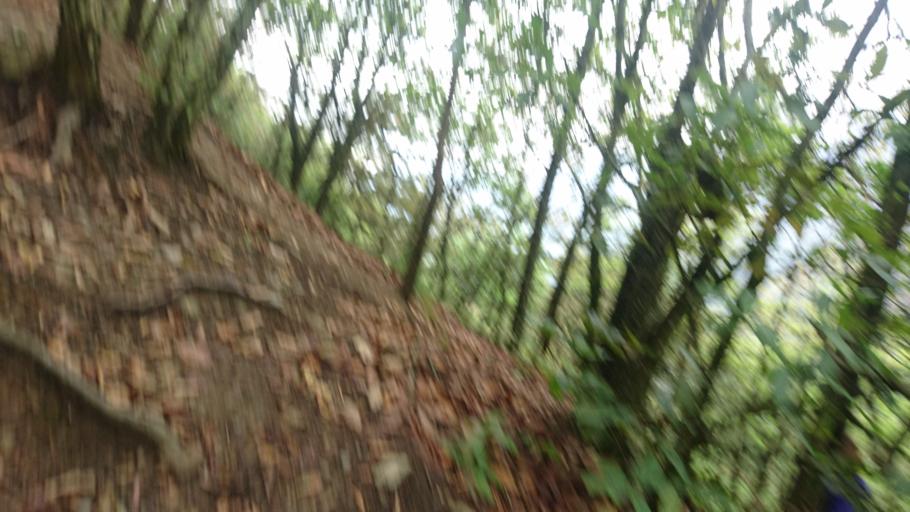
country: MX
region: Nuevo Leon
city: Garza Garcia
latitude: 25.6014
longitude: -100.3334
